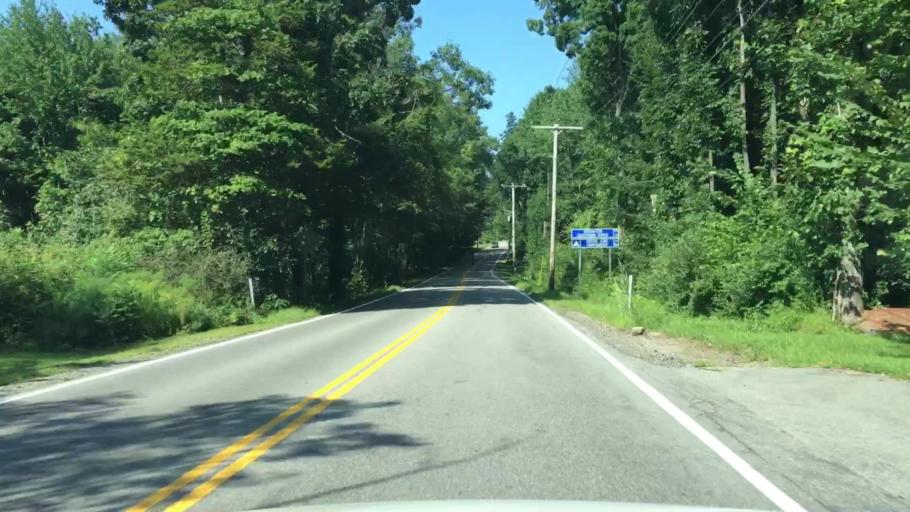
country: US
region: New Hampshire
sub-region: Rockingham County
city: Kensington
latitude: 42.9066
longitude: -70.9205
